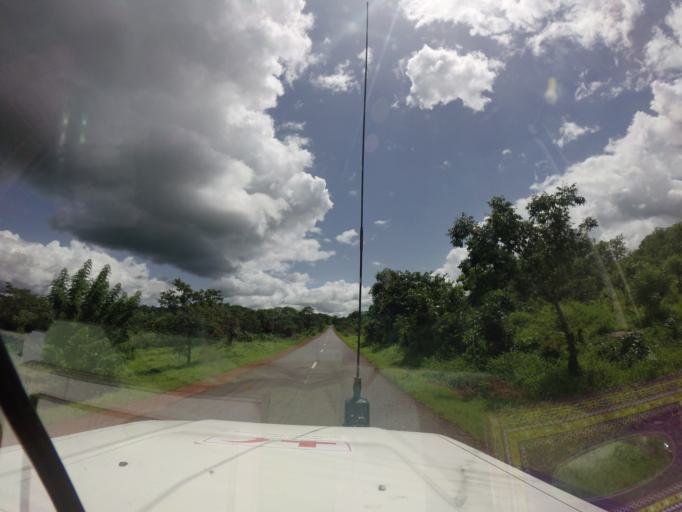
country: SL
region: Northern Province
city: Bindi
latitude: 10.1461
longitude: -11.5761
